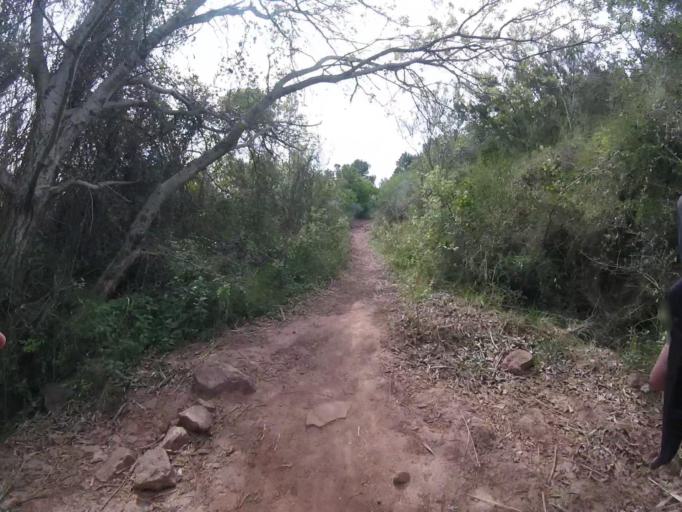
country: ES
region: Valencia
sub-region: Provincia de Castello
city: Benicassim
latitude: 40.0738
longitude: 0.0352
